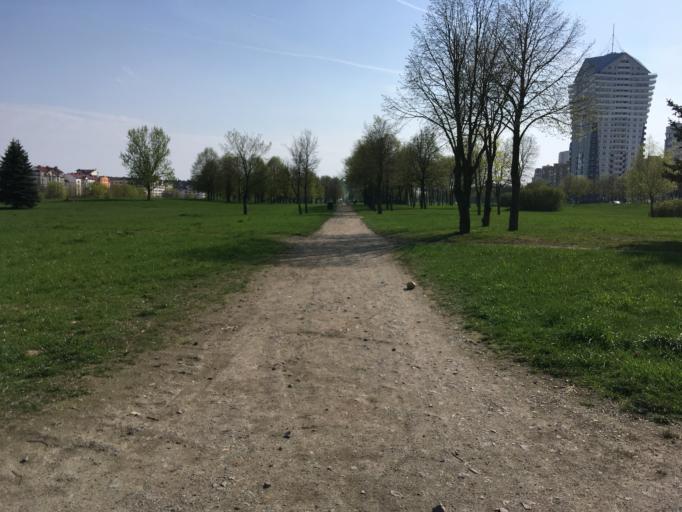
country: BY
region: Minsk
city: Minsk
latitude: 53.9264
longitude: 27.6410
